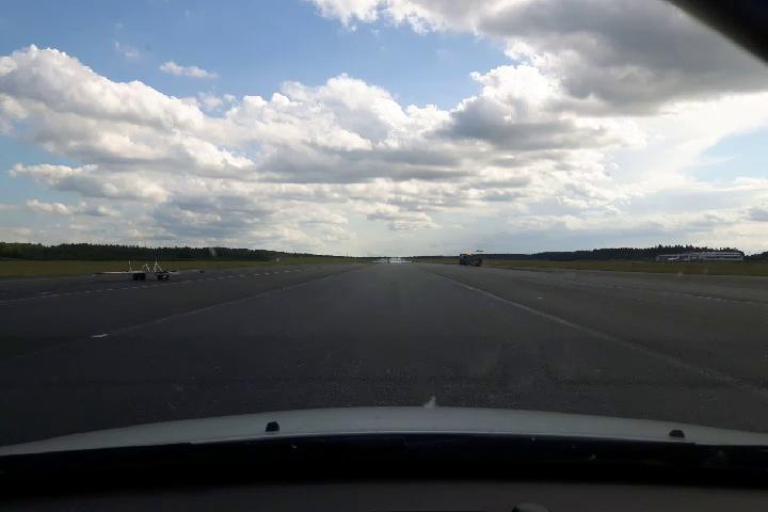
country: SE
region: Stockholm
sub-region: Sigtuna Kommun
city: Rosersberg
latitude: 59.6434
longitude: 17.9568
